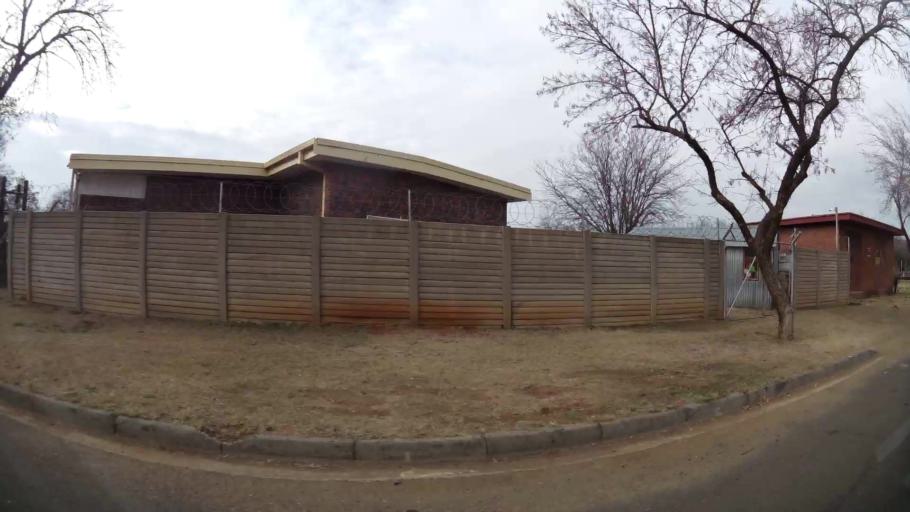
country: ZA
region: Orange Free State
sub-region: Mangaung Metropolitan Municipality
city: Bloemfontein
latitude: -29.1206
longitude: 26.1928
